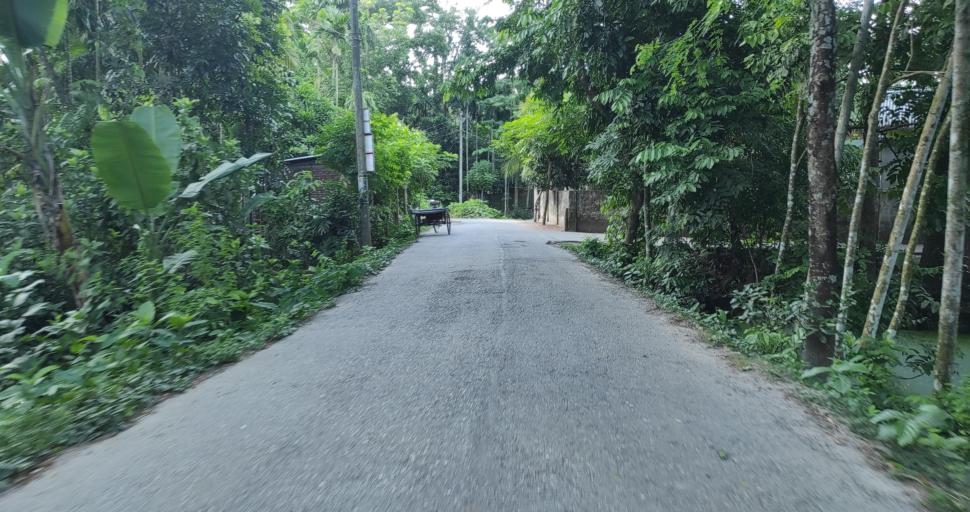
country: BD
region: Barisal
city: Gaurnadi
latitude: 22.8959
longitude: 90.1842
